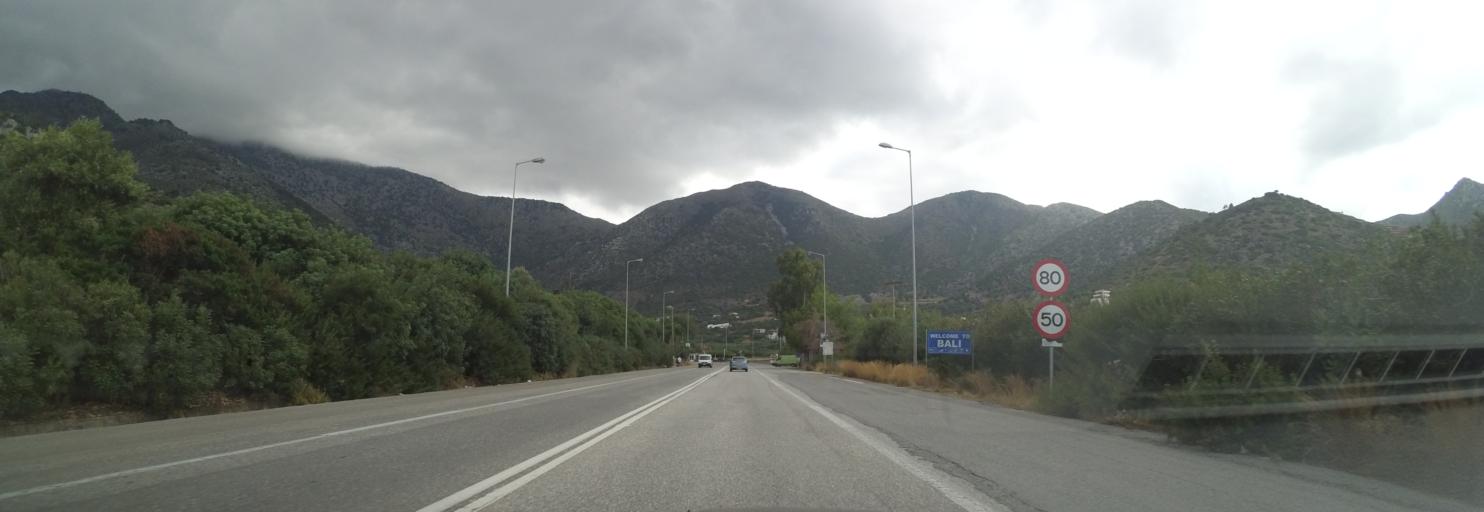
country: GR
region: Crete
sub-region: Nomos Rethymnis
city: Perama
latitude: 35.4036
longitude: 24.7875
